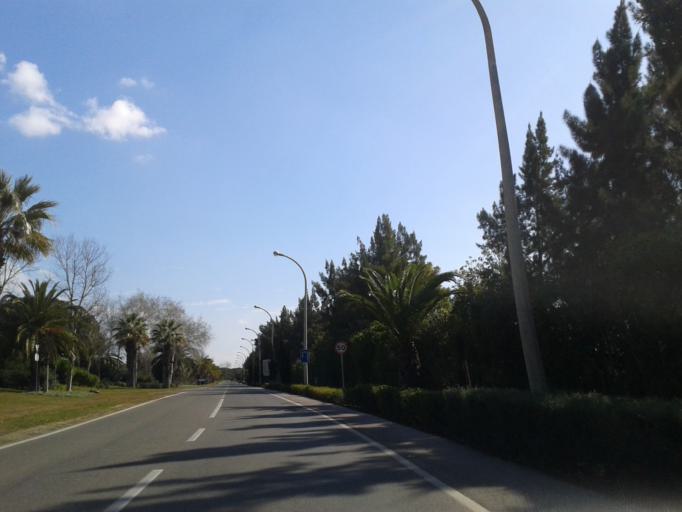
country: PT
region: Faro
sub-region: Loule
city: Vilamoura
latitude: 37.0925
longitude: -8.1274
